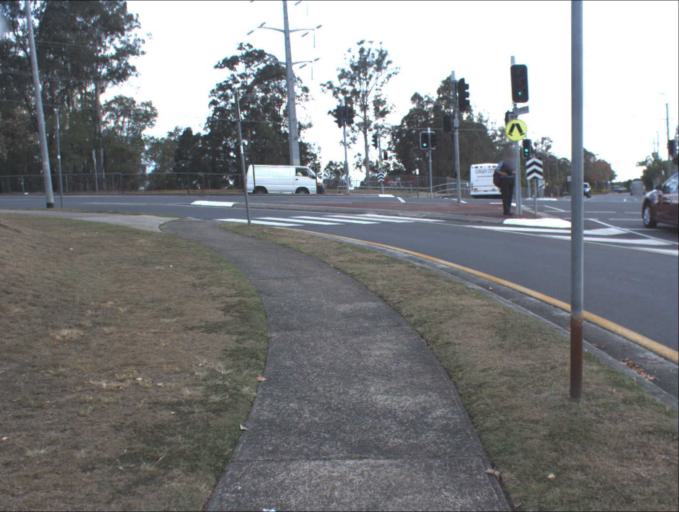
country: AU
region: Queensland
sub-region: Logan
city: Slacks Creek
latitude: -27.6348
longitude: 153.1487
